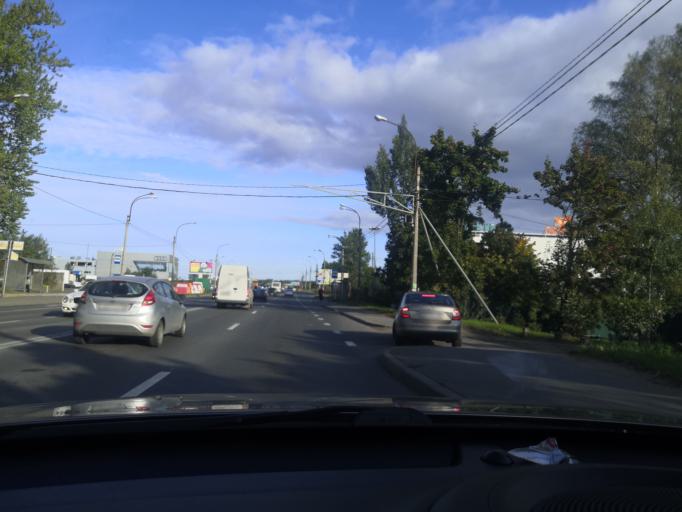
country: RU
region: St.-Petersburg
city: Pargolovo
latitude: 60.0921
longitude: 30.2577
